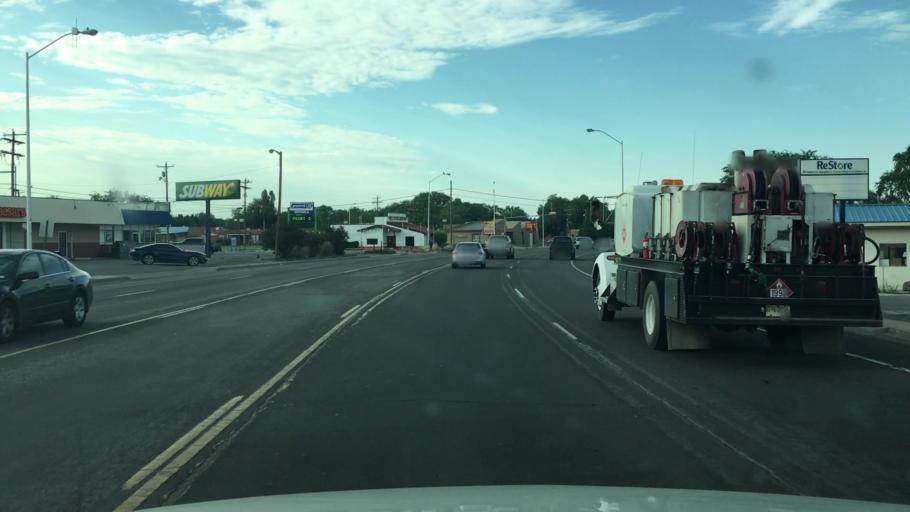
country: US
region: New Mexico
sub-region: Rio Arriba County
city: Espanola
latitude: 36.0017
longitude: -106.0631
